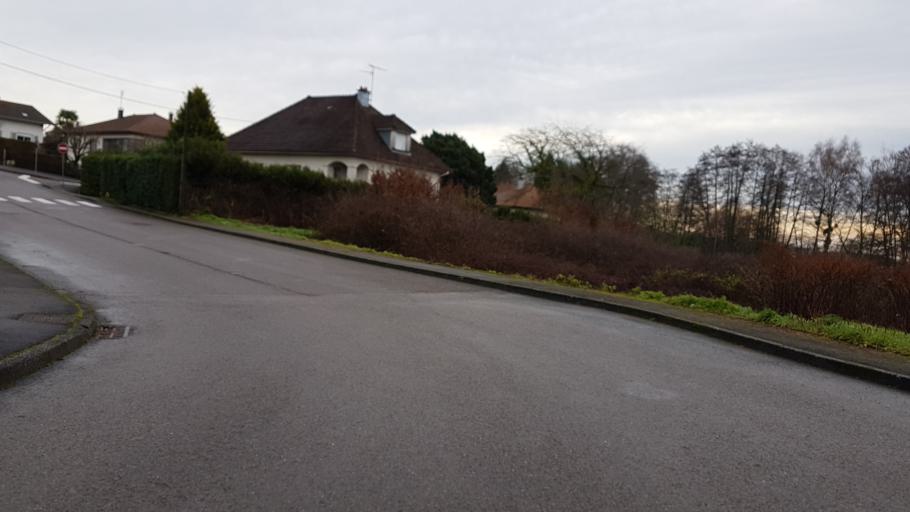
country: FR
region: Franche-Comte
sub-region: Departement de la Haute-Saone
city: Luxeuil-les-Bains
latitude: 47.8107
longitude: 6.3675
